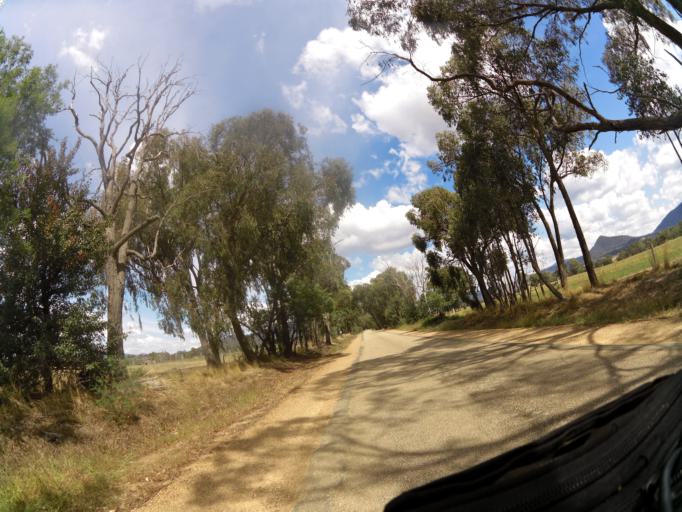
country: AU
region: Victoria
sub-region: Benalla
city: Benalla
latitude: -36.7589
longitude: 145.9776
